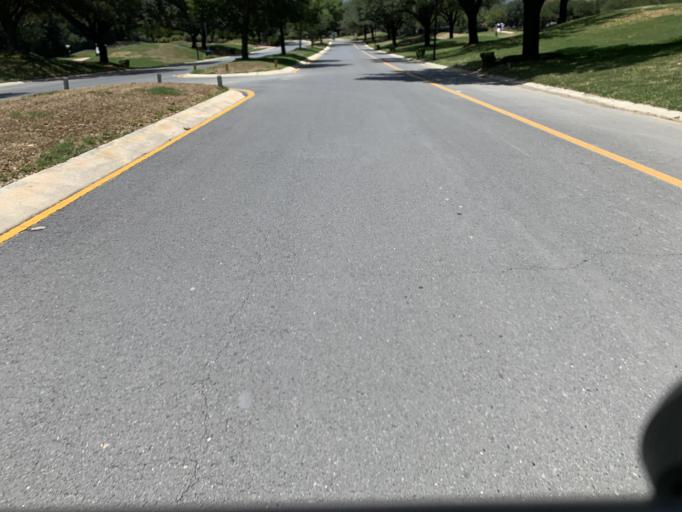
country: MX
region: Nuevo Leon
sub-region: Juarez
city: Bosques de San Pedro
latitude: 25.5179
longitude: -100.1949
